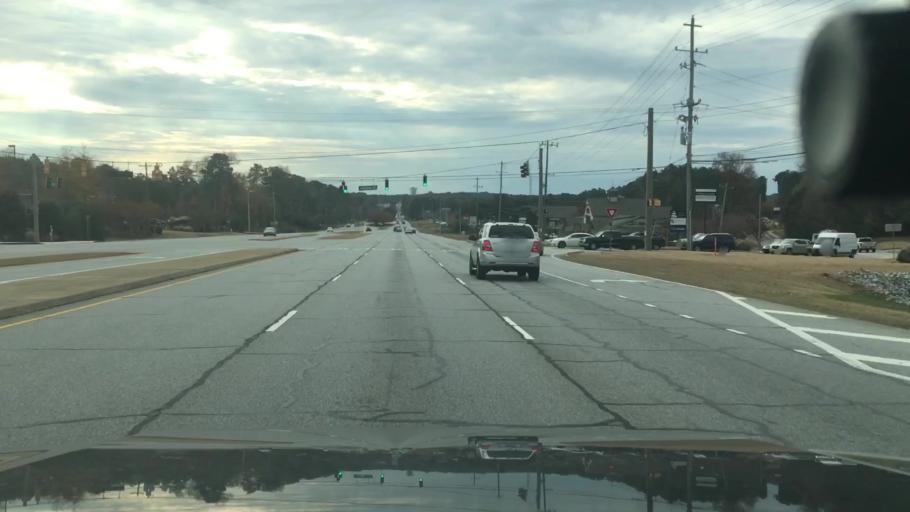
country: US
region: Georgia
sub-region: Coweta County
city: Newnan
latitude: 33.3947
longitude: -84.7633
